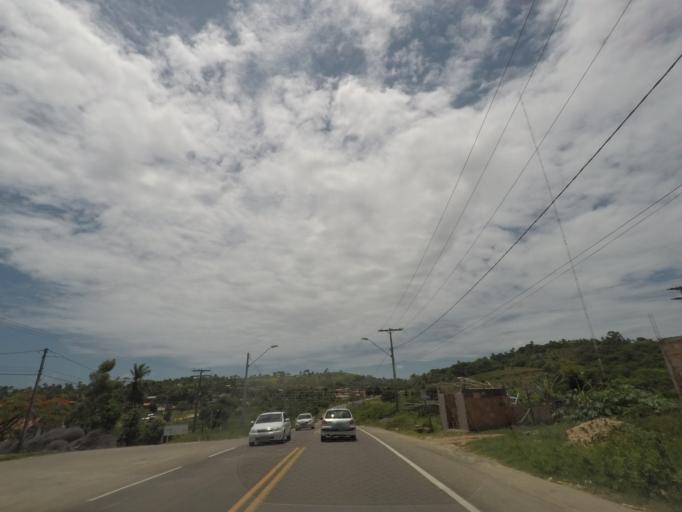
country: BR
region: Bahia
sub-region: Itaparica
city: Itaparica
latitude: -12.9348
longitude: -38.6242
